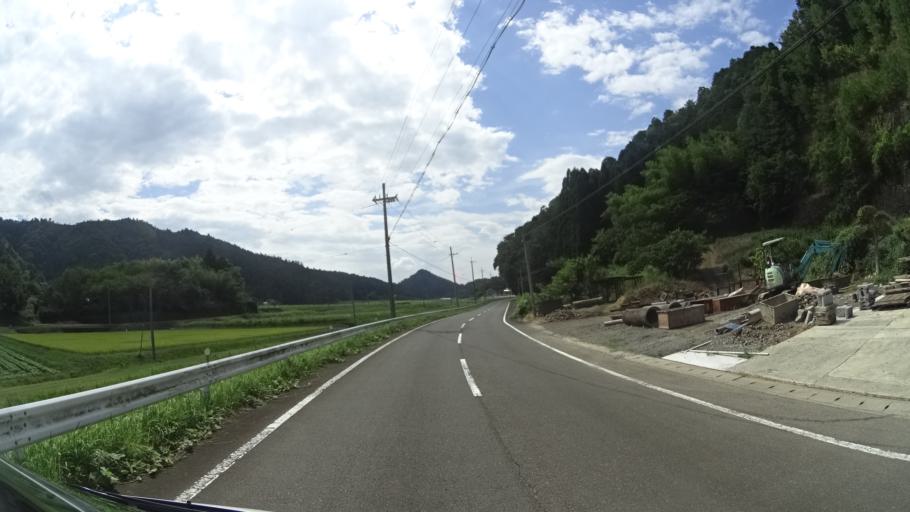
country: JP
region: Kyoto
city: Ayabe
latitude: 35.3690
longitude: 135.1898
